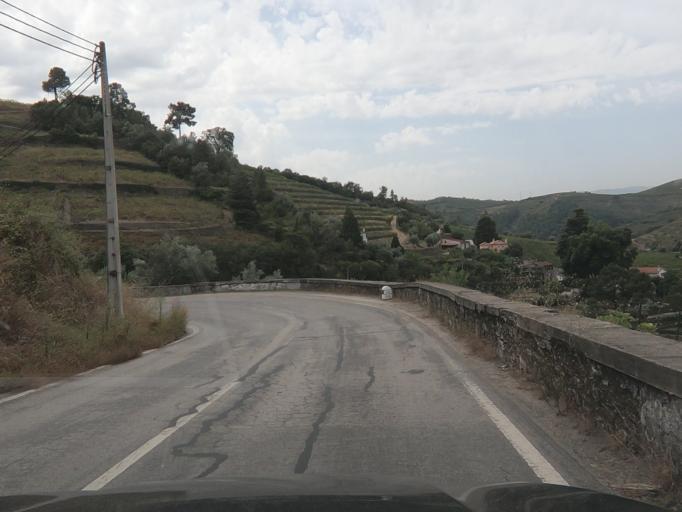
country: PT
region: Vila Real
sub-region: Santa Marta de Penaguiao
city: Santa Marta de Penaguiao
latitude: 41.2298
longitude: -7.7666
